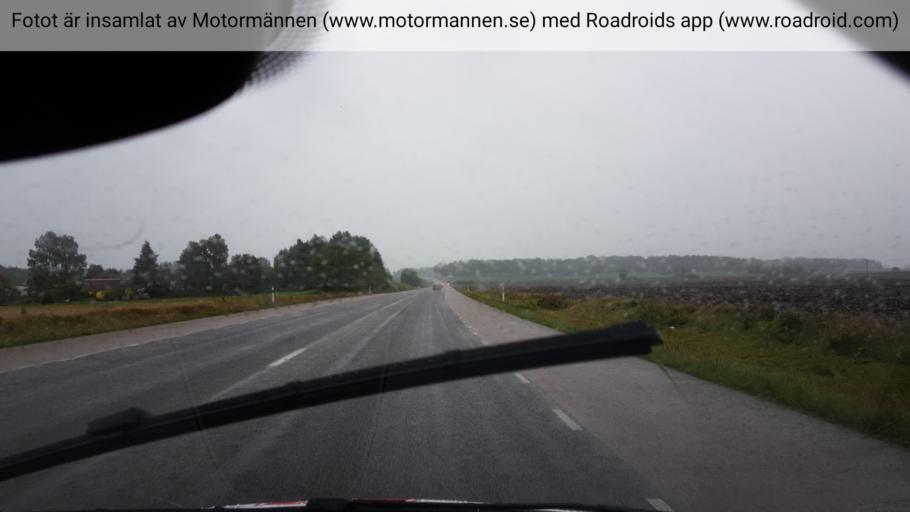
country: SE
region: Halland
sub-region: Laholms Kommun
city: Veinge
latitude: 56.5702
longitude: 13.0225
